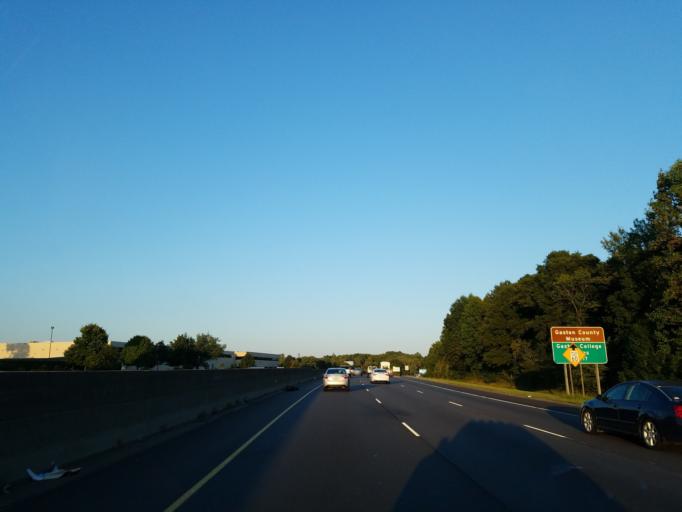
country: US
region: North Carolina
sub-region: Gaston County
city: Gastonia
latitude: 35.2853
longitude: -81.2032
